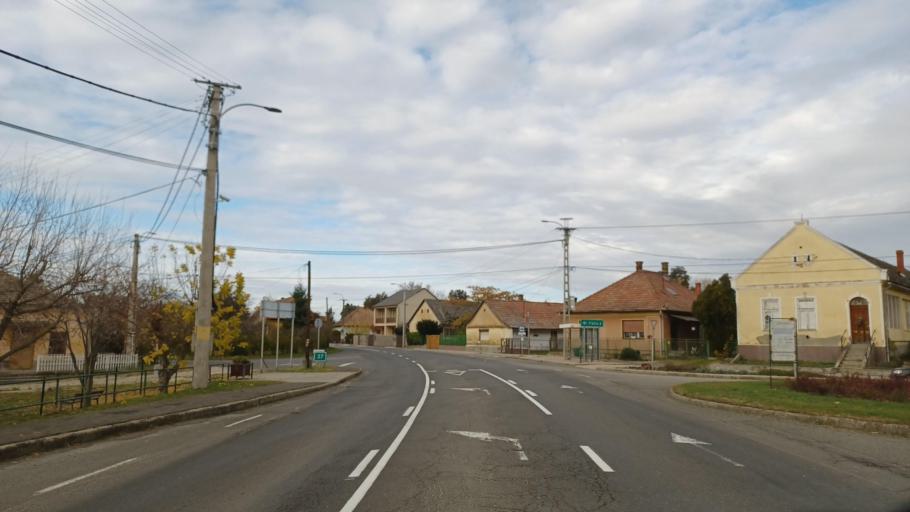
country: HU
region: Fejer
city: Cece
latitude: 46.7175
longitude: 18.6647
